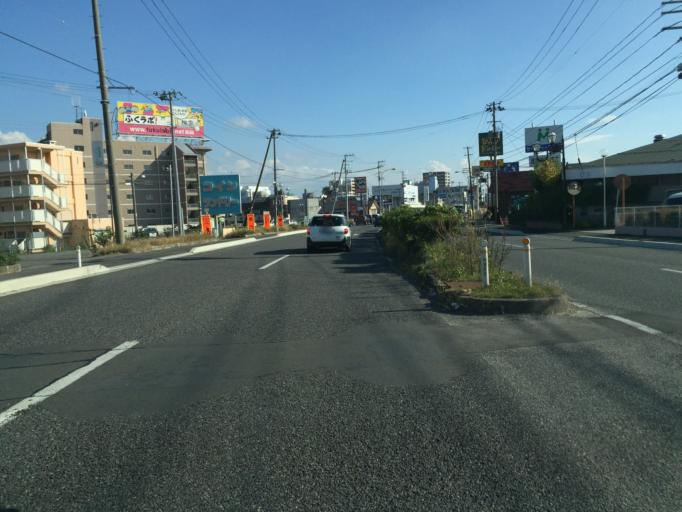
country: JP
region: Fukushima
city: Koriyama
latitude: 37.4100
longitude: 140.3499
